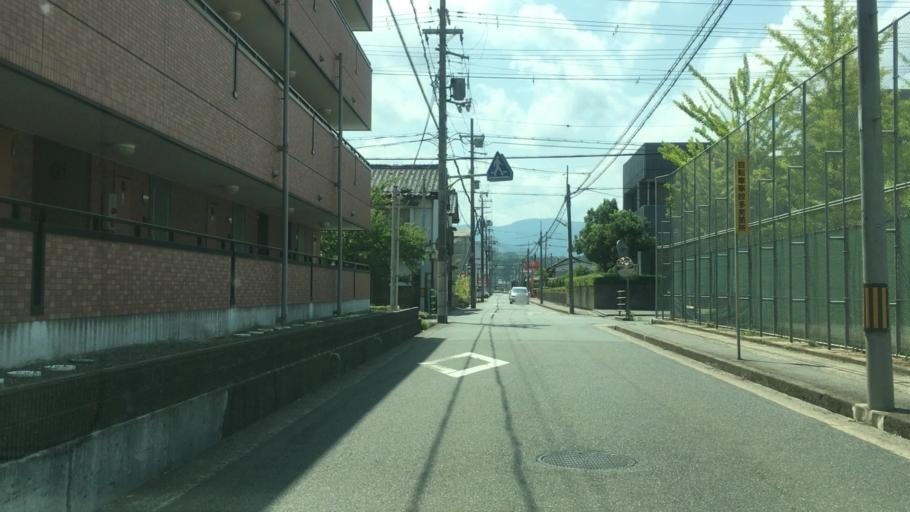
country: JP
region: Hyogo
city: Toyooka
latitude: 35.5490
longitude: 134.8194
